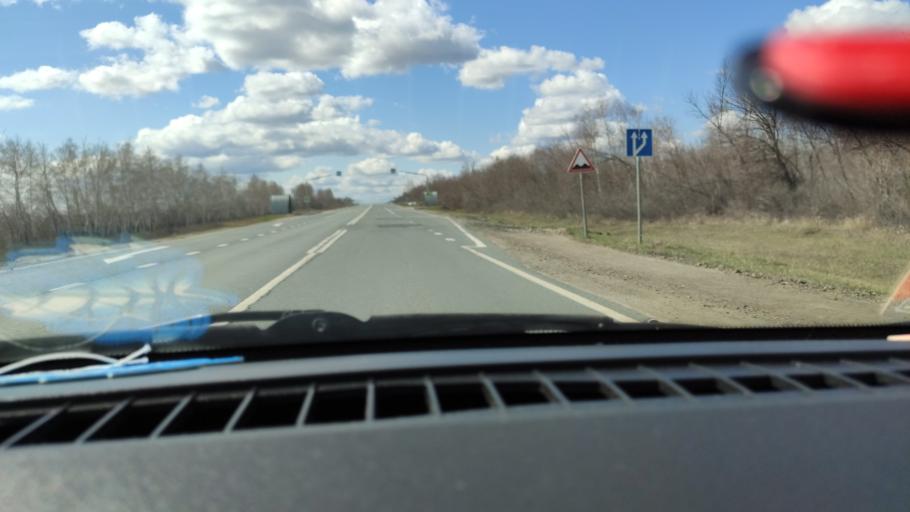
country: RU
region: Saratov
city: Dukhovnitskoye
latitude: 52.6792
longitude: 48.2308
